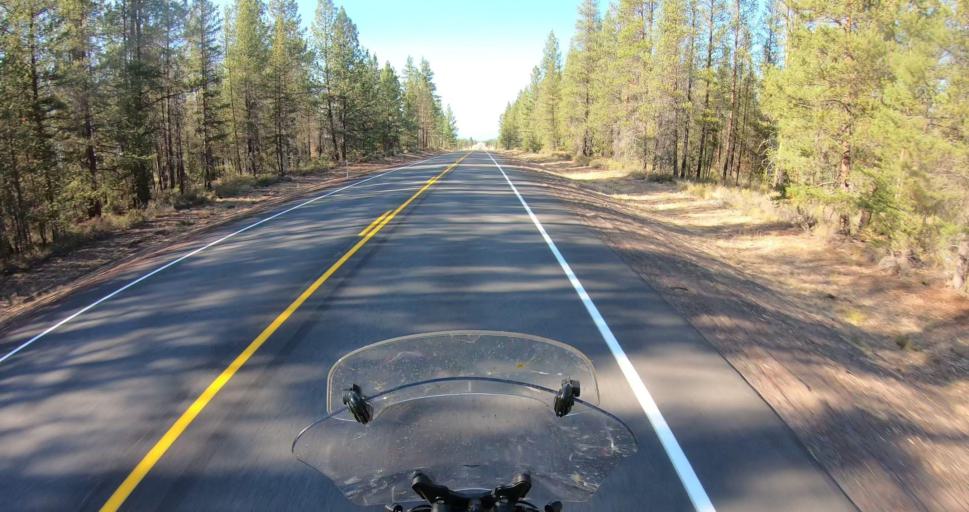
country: US
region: Oregon
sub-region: Deschutes County
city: La Pine
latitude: 43.5584
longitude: -121.4756
